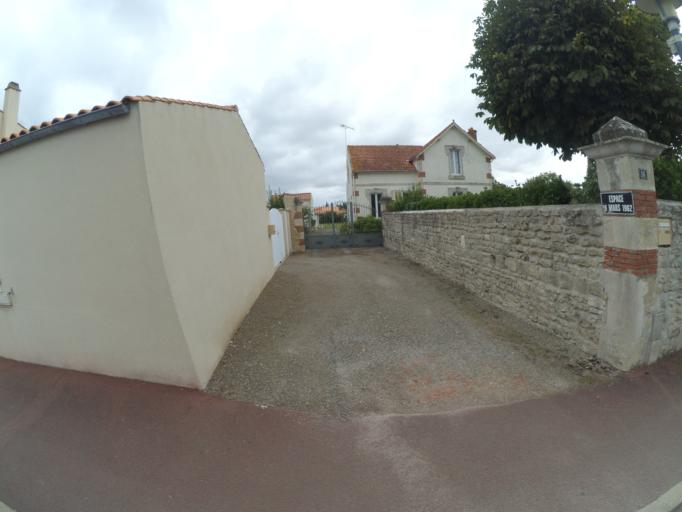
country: FR
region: Pays de la Loire
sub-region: Departement de la Vendee
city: Angles
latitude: 46.3980
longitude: -1.3051
